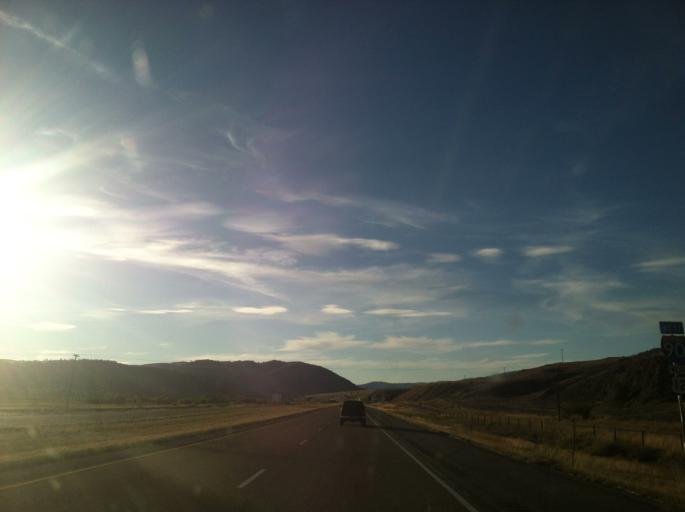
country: US
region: Montana
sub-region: Granite County
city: Philipsburg
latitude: 46.6742
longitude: -113.1645
